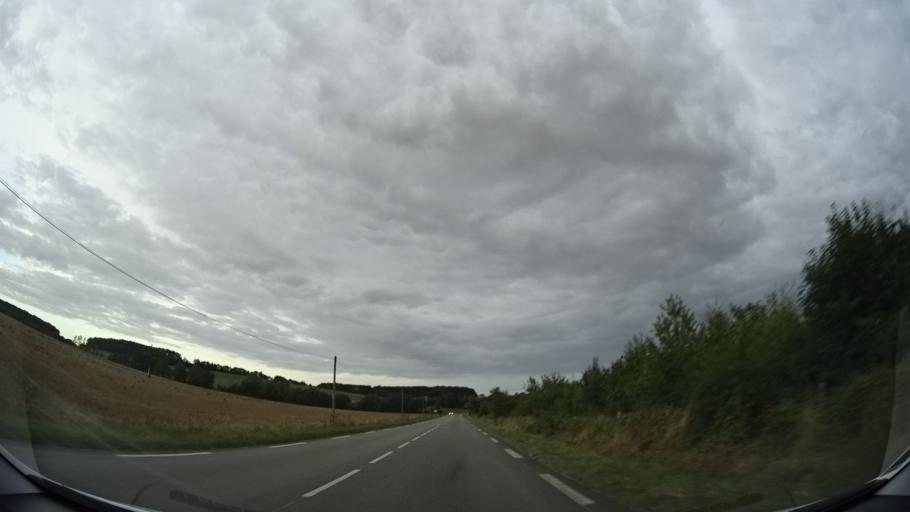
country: FR
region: Centre
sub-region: Departement du Loiret
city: Douchy
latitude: 47.9353
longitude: 3.0879
